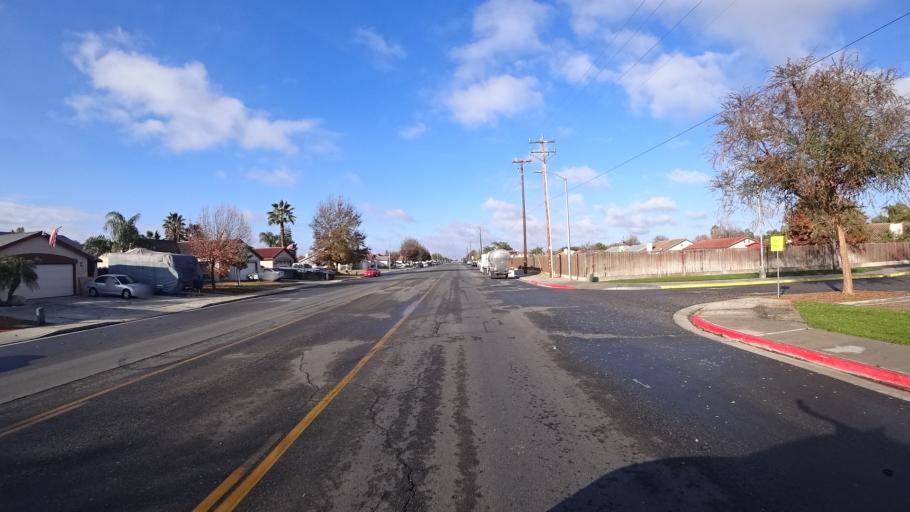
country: US
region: California
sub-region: Kern County
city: Greenfield
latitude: 35.2886
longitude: -119.0071
